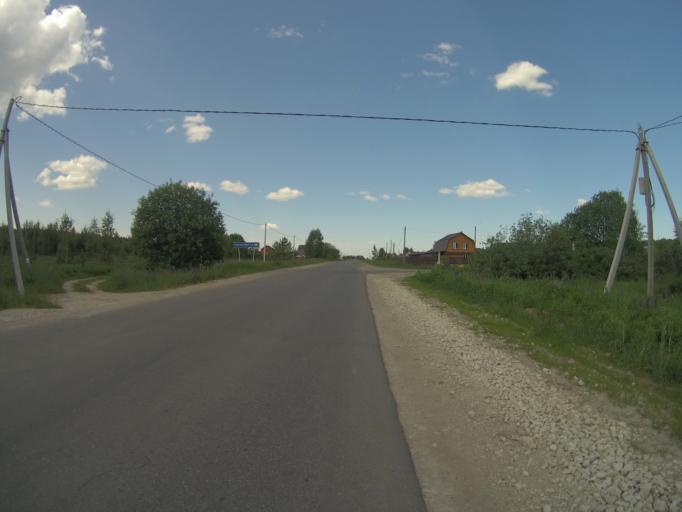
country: RU
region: Vladimir
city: Bogolyubovo
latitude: 56.2692
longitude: 40.5729
